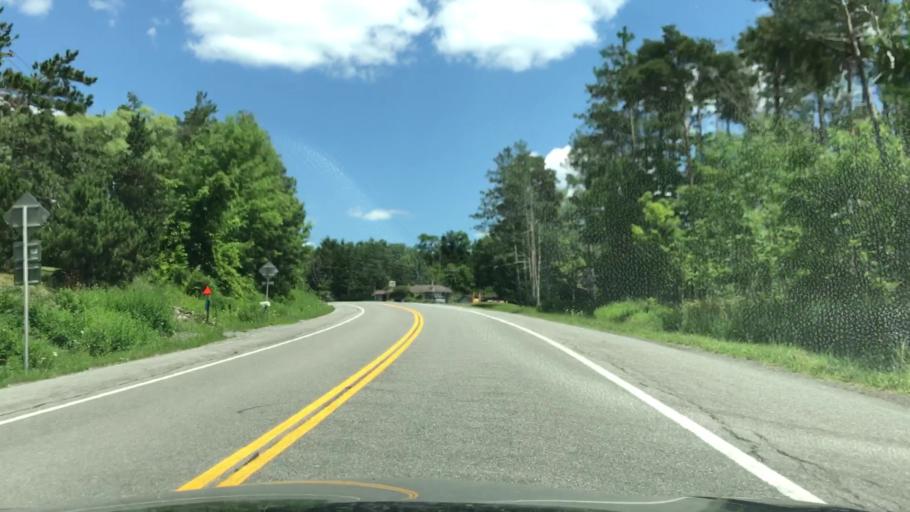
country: US
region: New York
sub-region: Erie County
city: East Aurora
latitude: 42.7648
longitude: -78.5110
